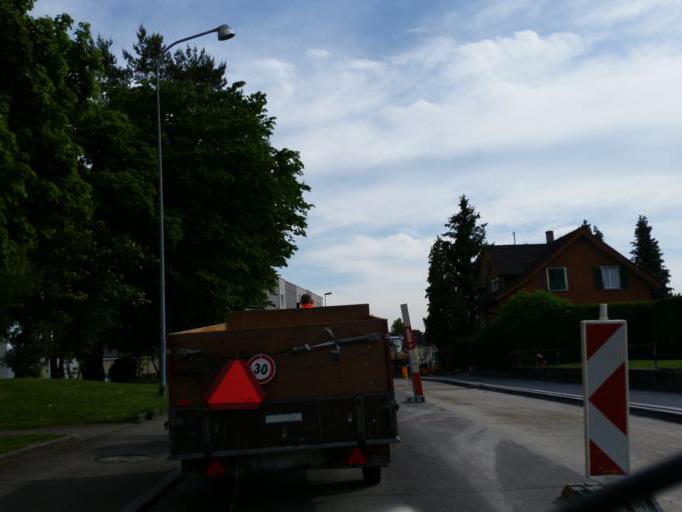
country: CH
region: Thurgau
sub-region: Arbon District
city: Amriswil
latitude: 47.5531
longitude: 9.3057
